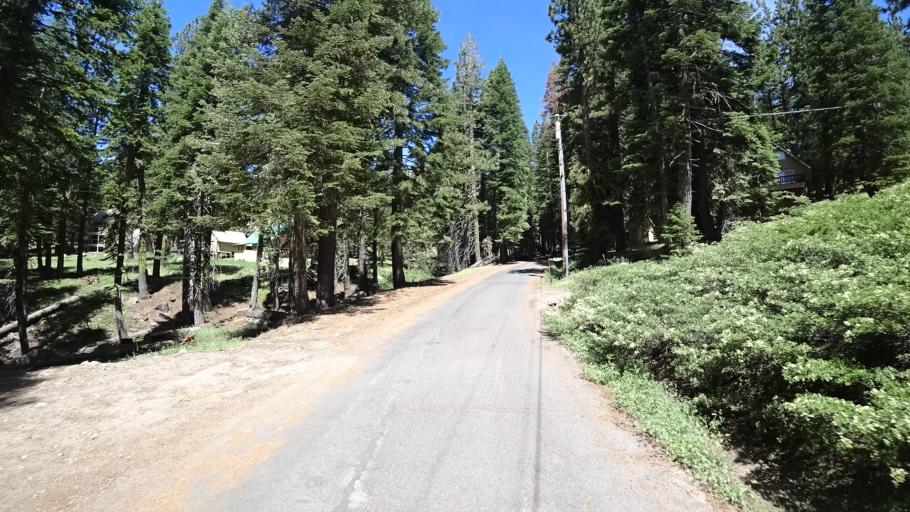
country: US
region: California
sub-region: Calaveras County
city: Arnold
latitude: 38.4285
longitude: -120.0989
